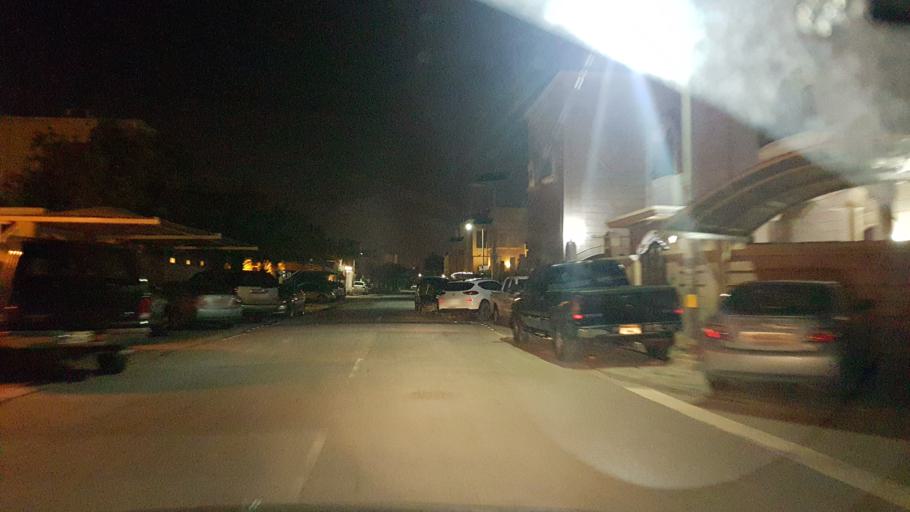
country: BH
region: Muharraq
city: Al Hadd
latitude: 26.2410
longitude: 50.6506
